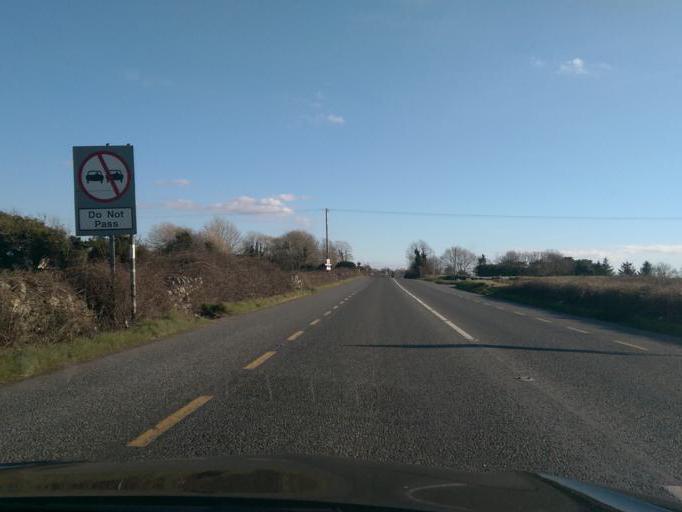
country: IE
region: Connaught
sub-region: County Galway
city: Oranmore
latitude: 53.2202
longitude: -8.8741
